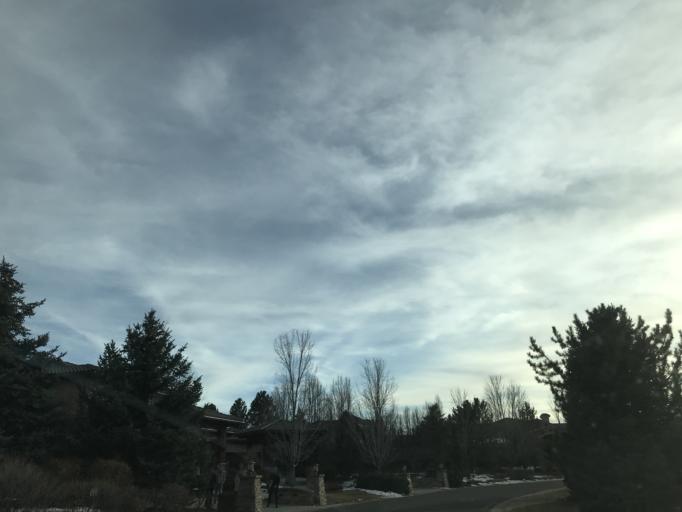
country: US
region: Colorado
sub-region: Arapahoe County
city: Columbine Valley
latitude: 39.6102
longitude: -105.0304
